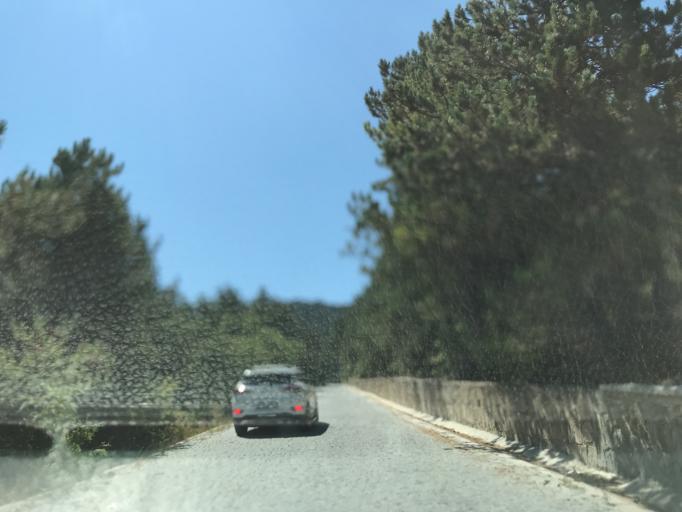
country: TR
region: Yozgat
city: Yozgat
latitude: 39.8079
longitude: 34.8088
